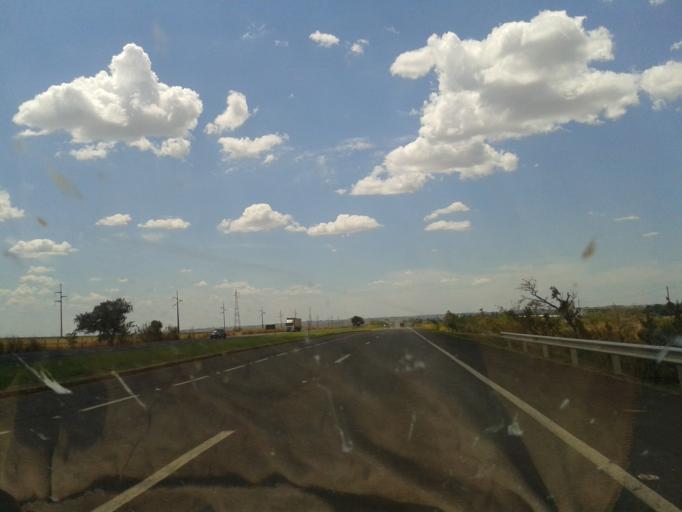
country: BR
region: Minas Gerais
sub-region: Uberlandia
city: Uberlandia
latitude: -19.0482
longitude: -48.1969
